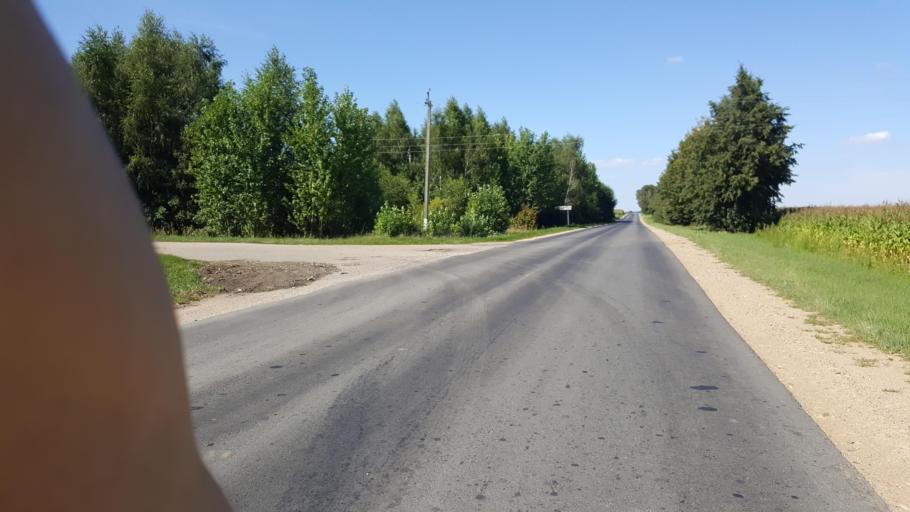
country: BY
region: Brest
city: Charnawchytsy
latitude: 52.2826
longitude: 23.6034
